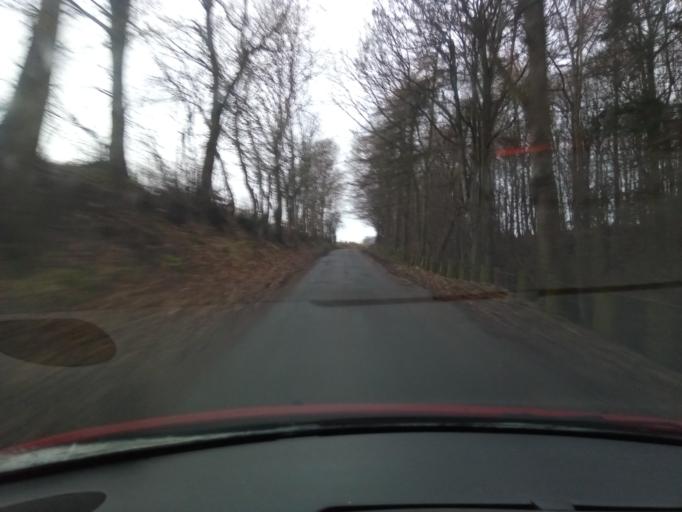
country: GB
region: Scotland
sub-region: The Scottish Borders
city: Kelso
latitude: 55.5427
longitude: -2.4368
